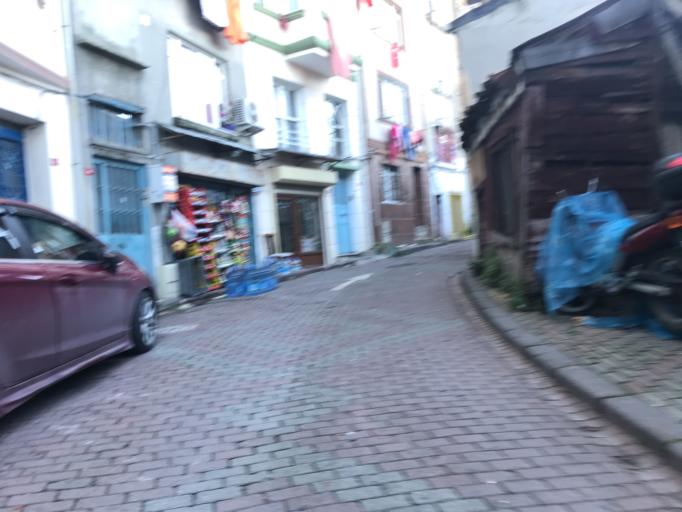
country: TR
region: Istanbul
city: Istanbul
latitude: 41.0281
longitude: 28.9524
